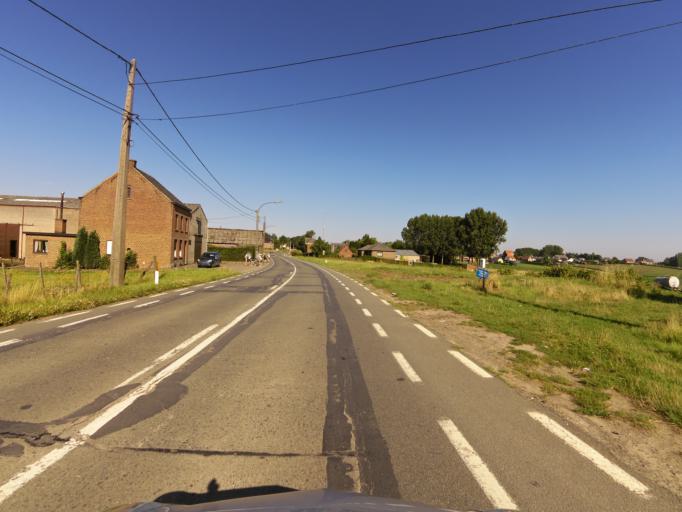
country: BE
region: Flanders
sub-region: Provincie Oost-Vlaanderen
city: Oudenaarde
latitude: 50.8275
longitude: 3.6843
